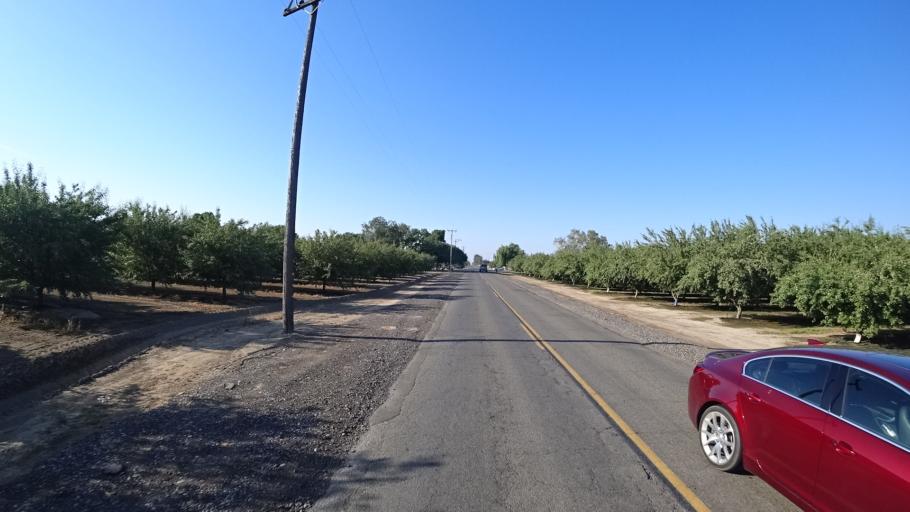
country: US
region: California
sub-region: Kings County
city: Lemoore
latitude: 36.2854
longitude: -119.7447
